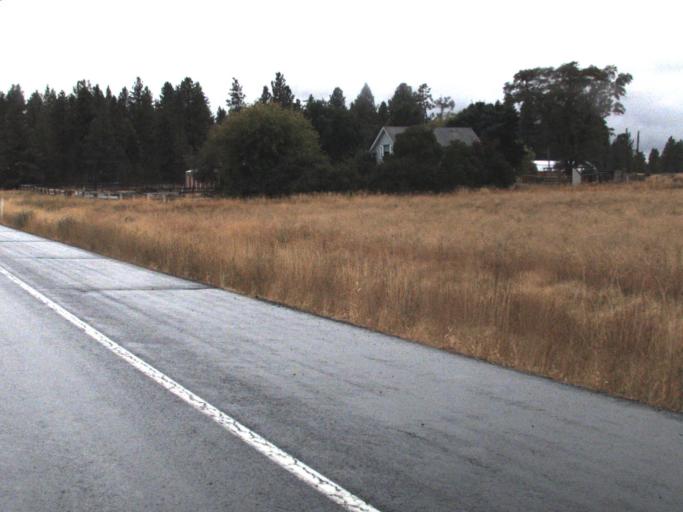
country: US
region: Washington
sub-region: Spokane County
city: Spokane
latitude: 47.5109
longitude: -117.4006
